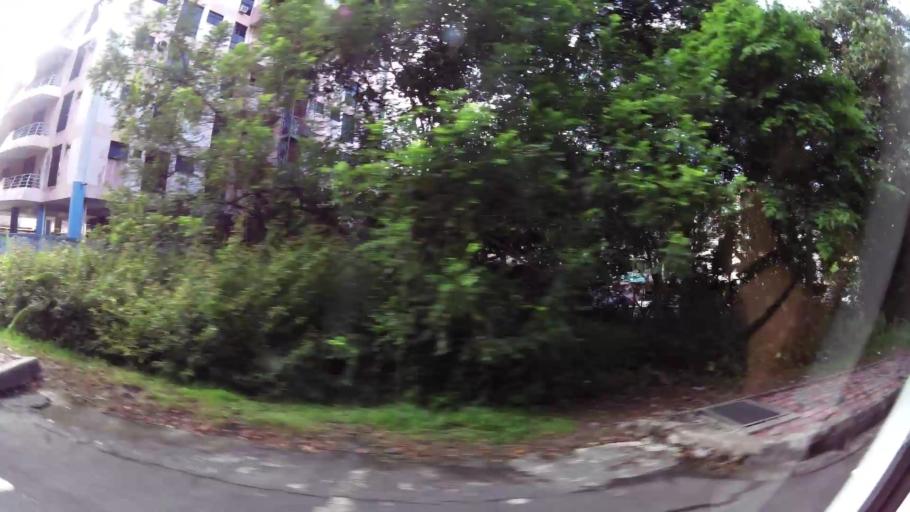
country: BN
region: Brunei and Muara
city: Bandar Seri Begawan
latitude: 4.8919
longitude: 114.9479
